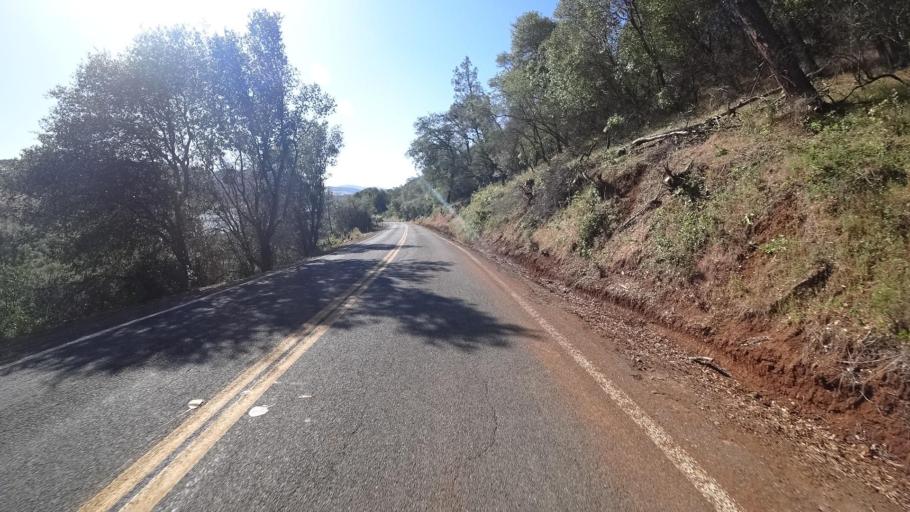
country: US
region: California
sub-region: Lake County
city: Clearlake Oaks
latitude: 38.9907
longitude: -122.6888
